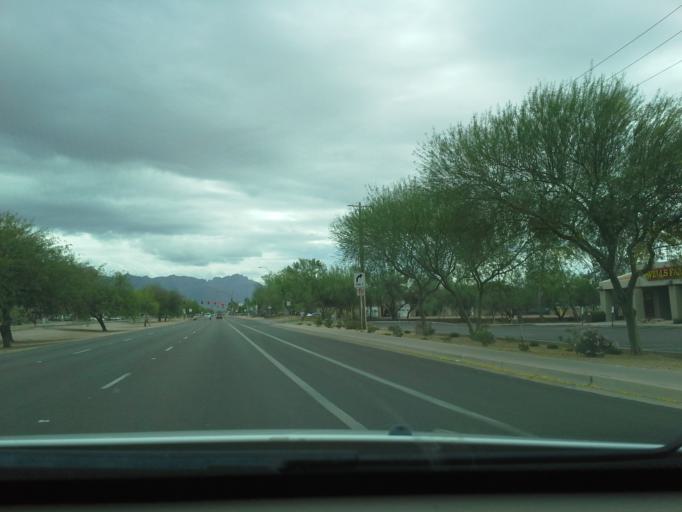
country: US
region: Arizona
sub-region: Pinal County
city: Apache Junction
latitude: 33.4150
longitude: -111.5774
